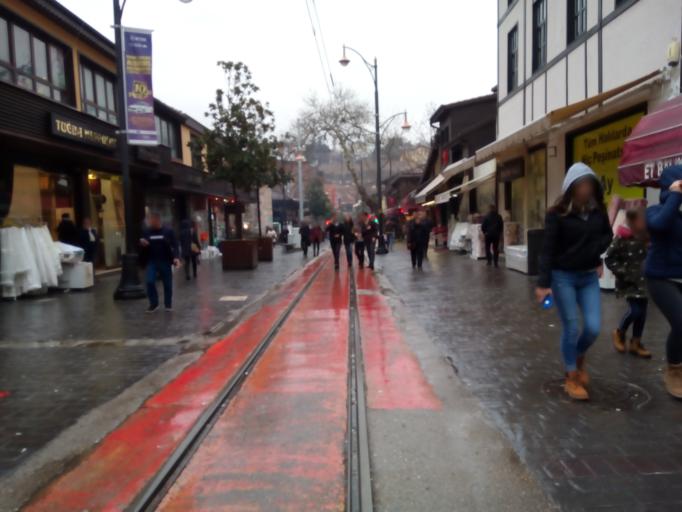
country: TR
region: Bursa
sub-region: Osmangazi
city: Bursa
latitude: 40.1860
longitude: 29.0616
